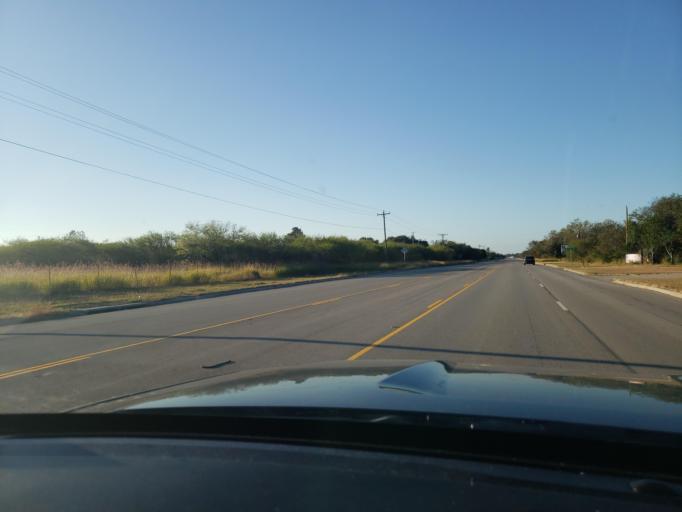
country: US
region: Texas
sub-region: Bee County
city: Beeville
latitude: 28.4346
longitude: -97.7137
